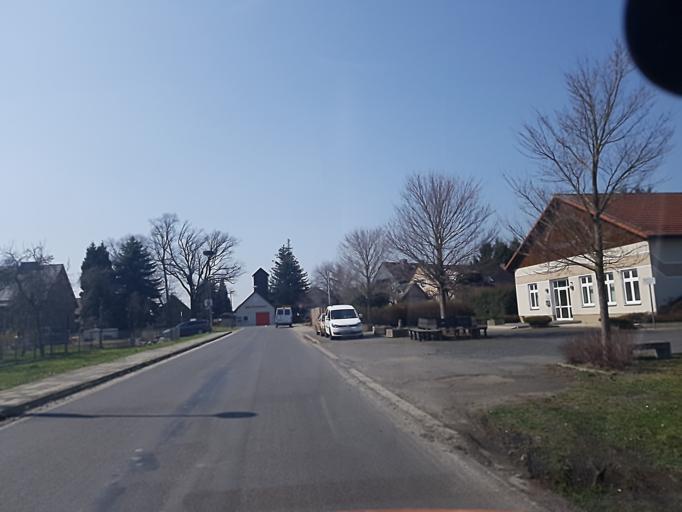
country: DE
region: Saxony
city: Gross Duben
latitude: 51.6756
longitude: 14.5375
